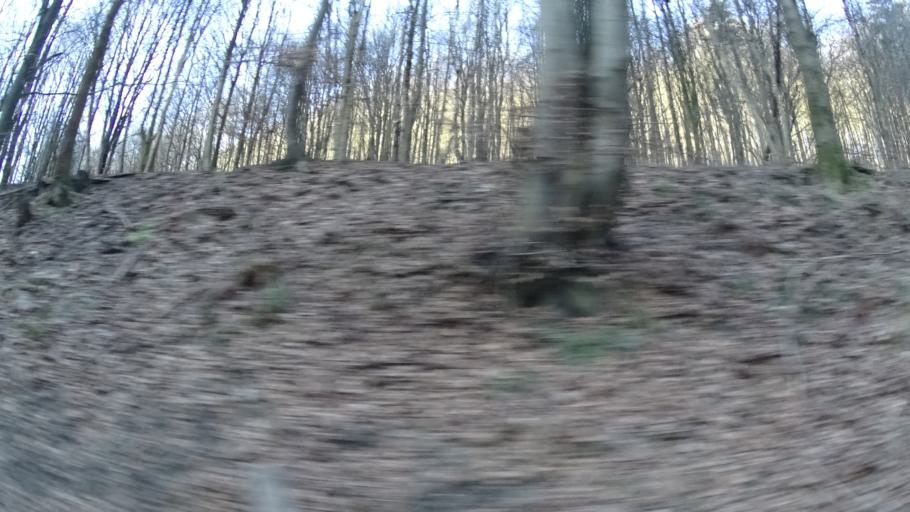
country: DE
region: Bavaria
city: Foritz
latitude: 50.3684
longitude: 11.2150
